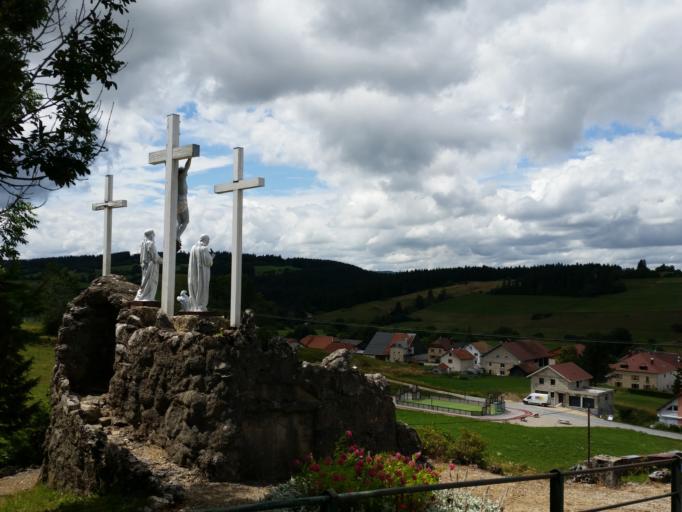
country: FR
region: Franche-Comte
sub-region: Departement du Doubs
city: Jougne
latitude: 46.7524
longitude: 6.3189
